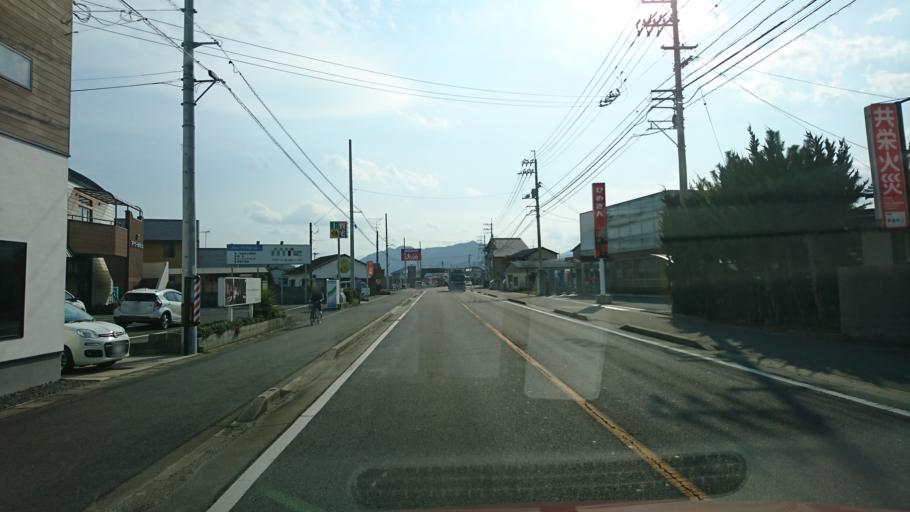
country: JP
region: Ehime
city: Saijo
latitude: 34.0243
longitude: 133.0381
